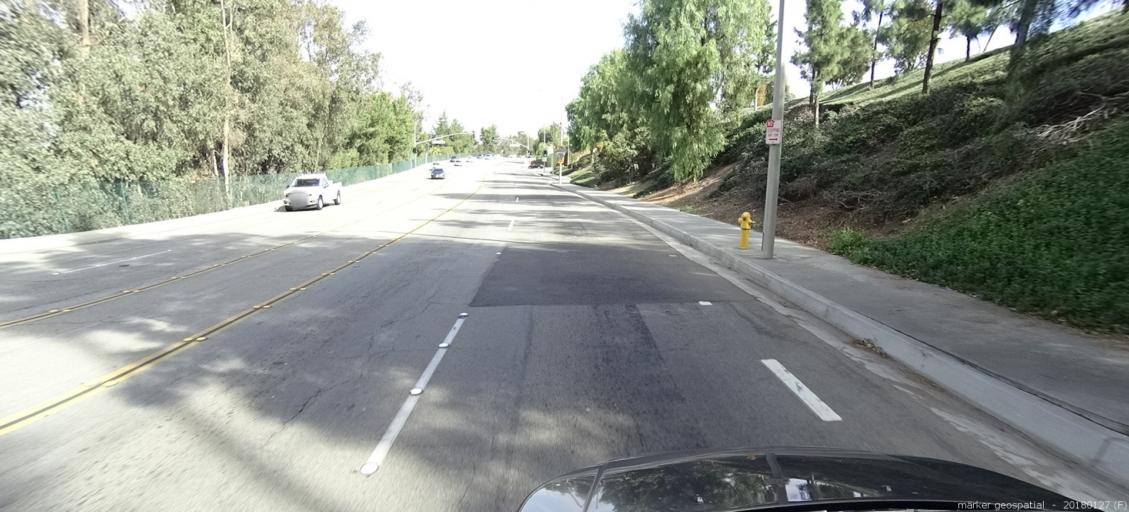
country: US
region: California
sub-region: Los Angeles County
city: Diamond Bar
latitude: 34.0040
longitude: -117.8240
